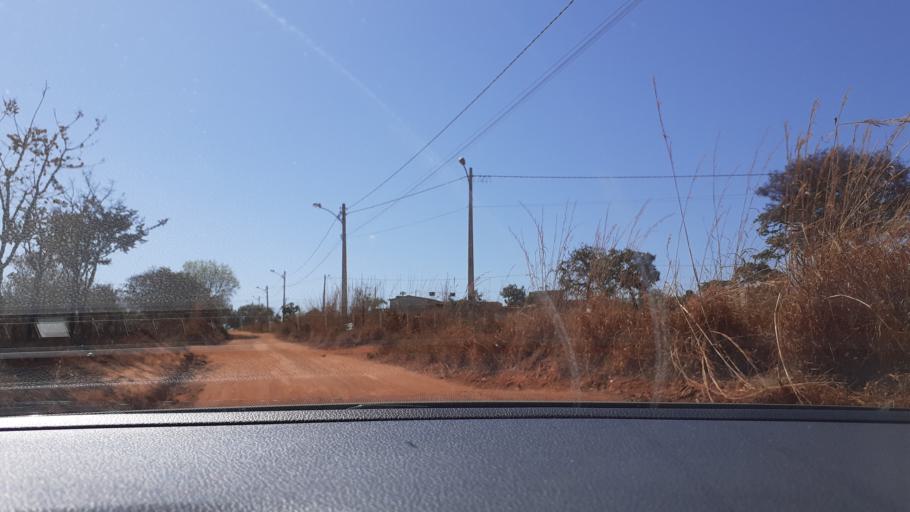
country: BR
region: Goias
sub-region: Aparecida De Goiania
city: Aparecida de Goiania
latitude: -16.8898
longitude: -49.2604
